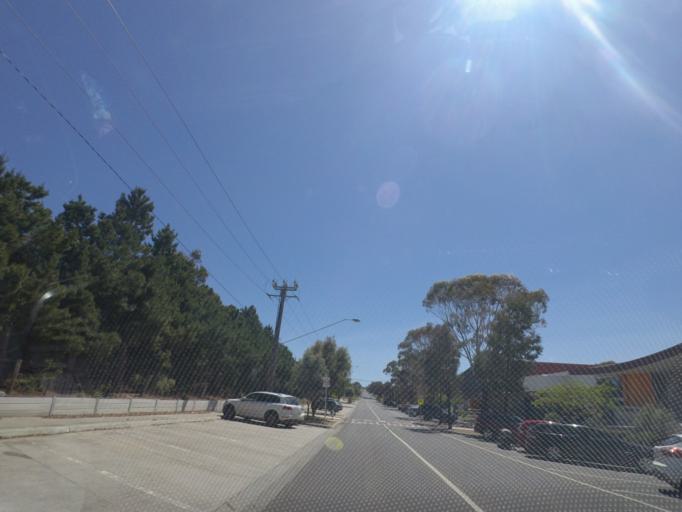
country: AU
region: Victoria
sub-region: Hume
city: Sunbury
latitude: -37.5827
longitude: 144.6927
